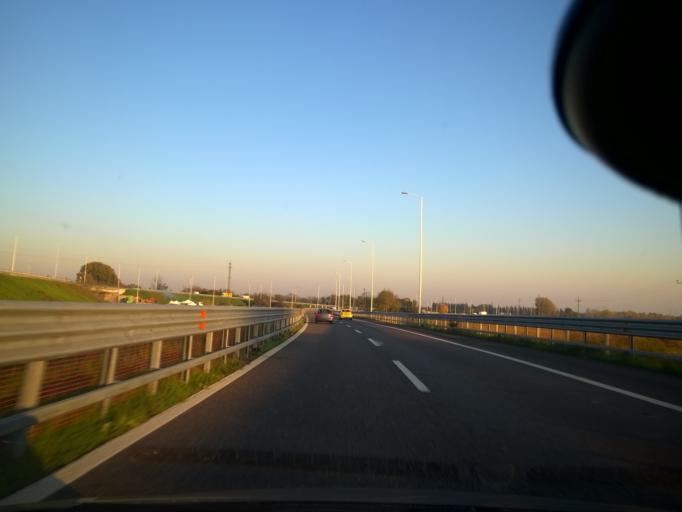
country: IT
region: Lombardy
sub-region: Citta metropolitana di Milano
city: Civesio
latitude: 45.3783
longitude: 9.2736
